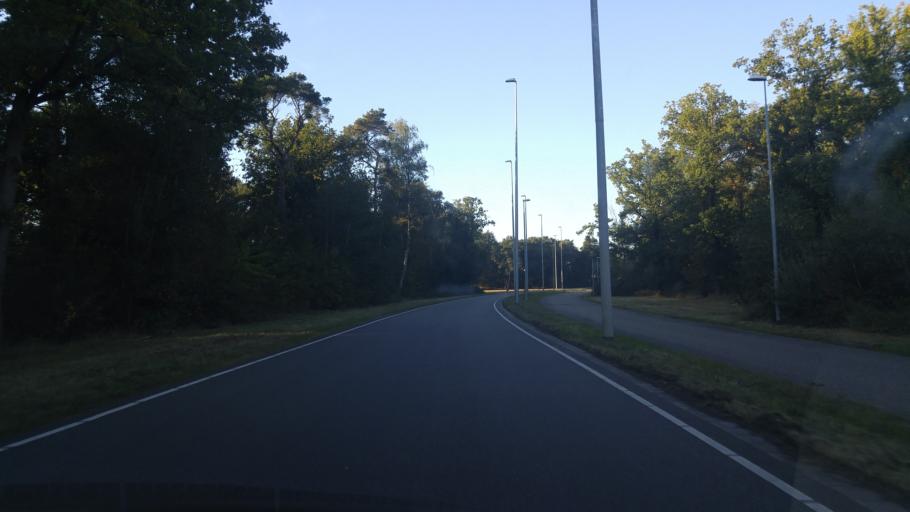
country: NL
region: North Brabant
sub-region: Gemeente Eindhoven
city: Meerhoven
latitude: 51.4414
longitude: 5.3894
